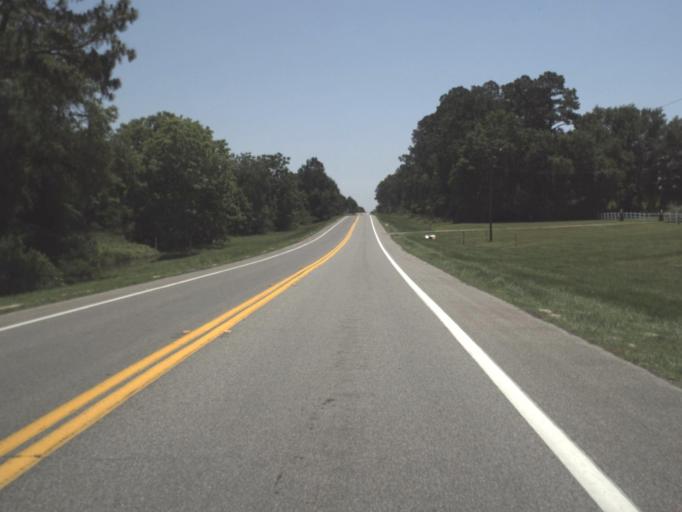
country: US
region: Florida
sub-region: Suwannee County
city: Live Oak
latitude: 30.3229
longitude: -83.0446
